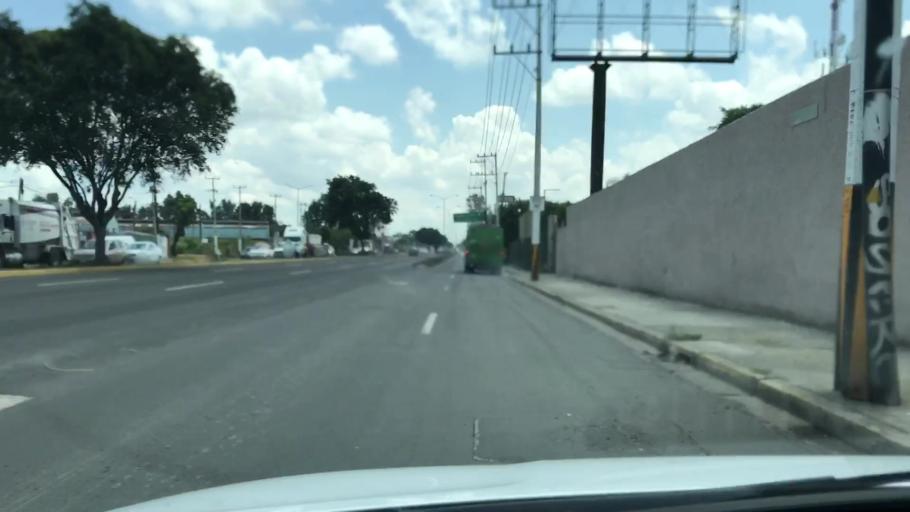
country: MX
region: Jalisco
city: Nuevo Mexico
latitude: 20.7546
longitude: -103.4260
